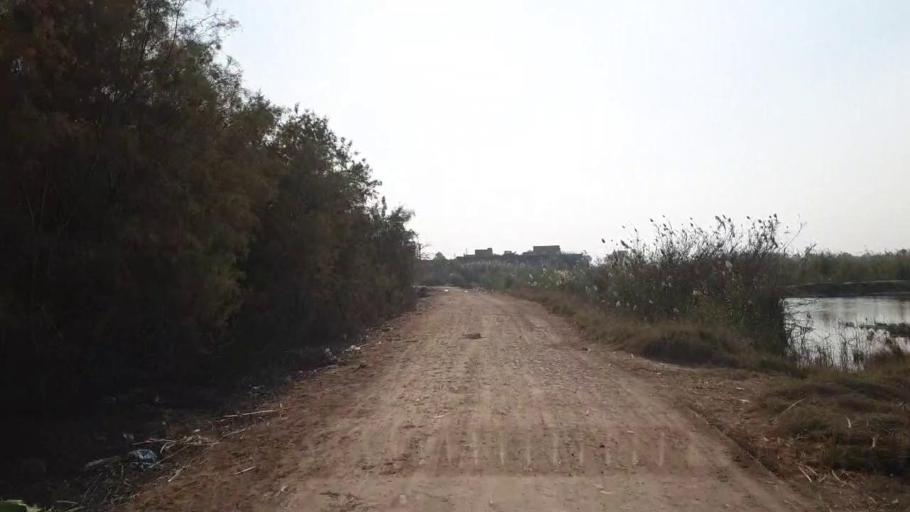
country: PK
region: Sindh
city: Tando Adam
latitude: 25.6775
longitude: 68.5656
